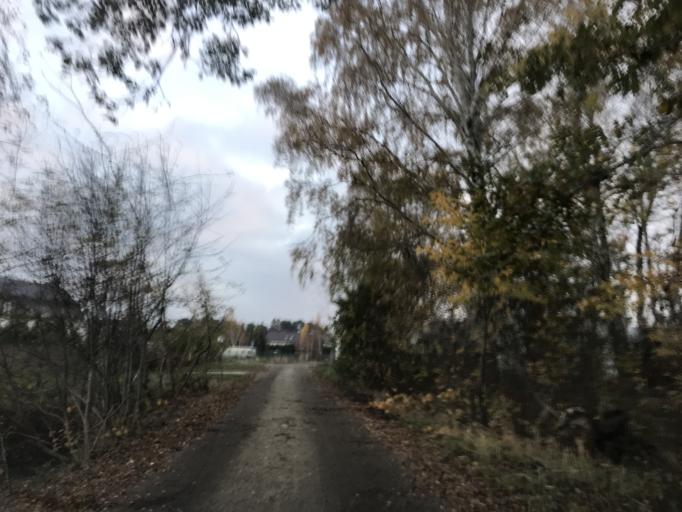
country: PL
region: Pomeranian Voivodeship
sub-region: Powiat pucki
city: Wierzchucino
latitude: 54.8248
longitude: 18.0831
